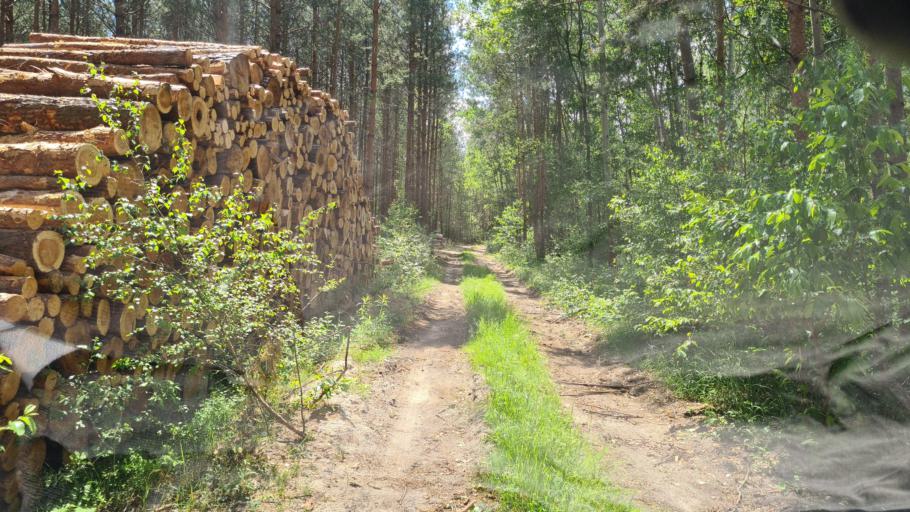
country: DE
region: Brandenburg
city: Sallgast
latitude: 51.5933
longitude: 13.8240
